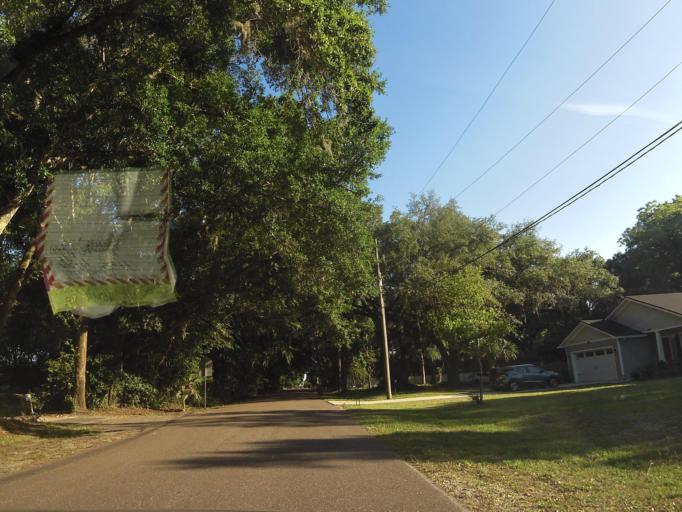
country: US
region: Florida
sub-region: Duval County
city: Jacksonville
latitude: 30.4628
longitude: -81.5665
